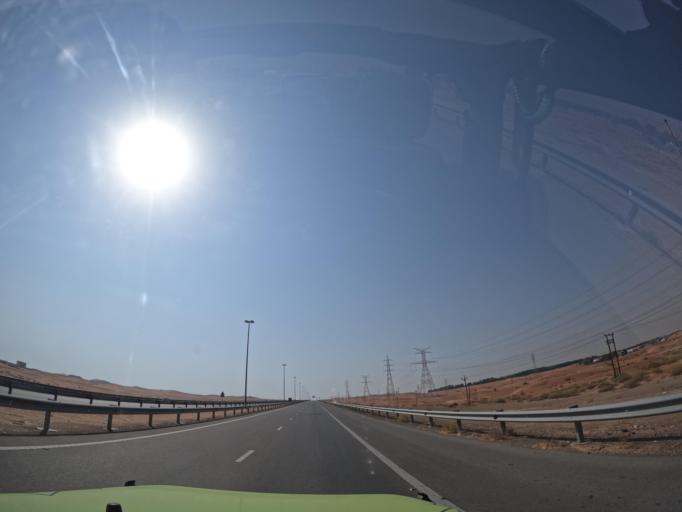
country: OM
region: Al Buraimi
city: Al Buraymi
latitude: 24.3551
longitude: 55.7345
